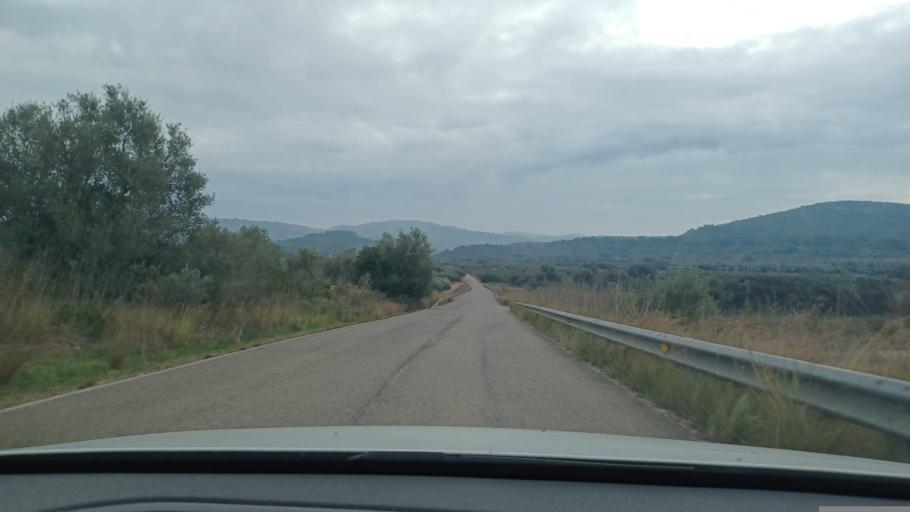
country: ES
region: Catalonia
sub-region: Provincia de Tarragona
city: Santa Barbara
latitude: 40.6665
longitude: 0.4513
